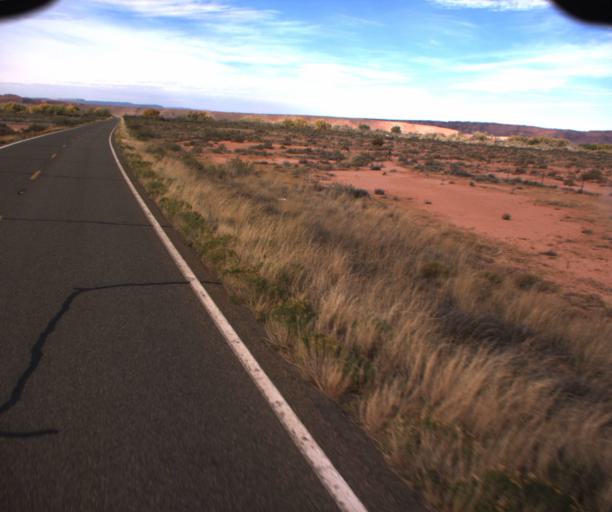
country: US
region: Arizona
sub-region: Apache County
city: Many Farms
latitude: 36.4657
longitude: -109.5818
